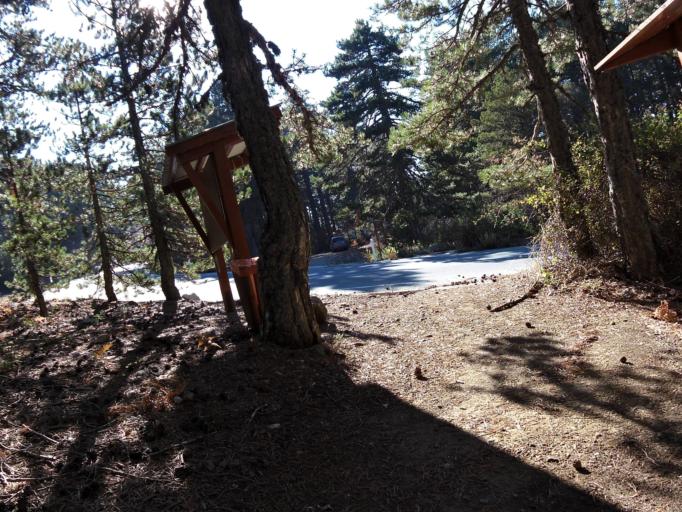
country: CY
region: Lefkosia
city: Kakopetria
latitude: 34.9478
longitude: 32.8474
